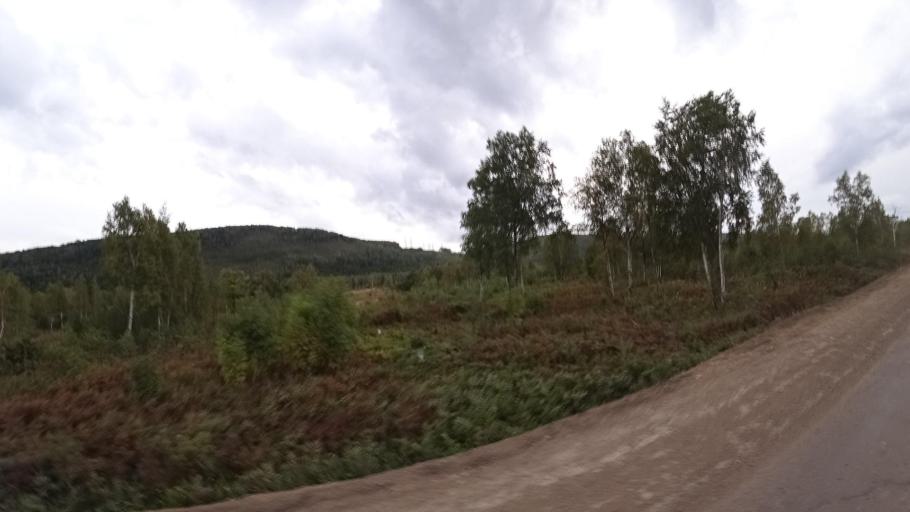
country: RU
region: Jewish Autonomous Oblast
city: Khingansk
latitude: 48.9915
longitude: 131.1063
